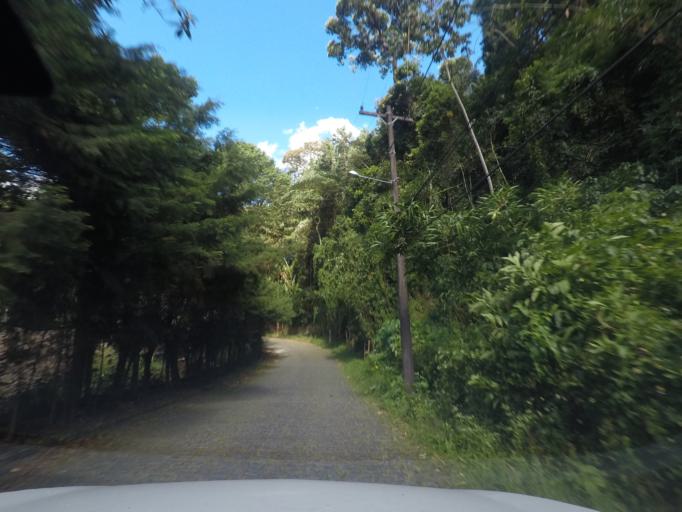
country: BR
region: Rio de Janeiro
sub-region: Teresopolis
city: Teresopolis
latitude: -22.4334
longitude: -42.9925
